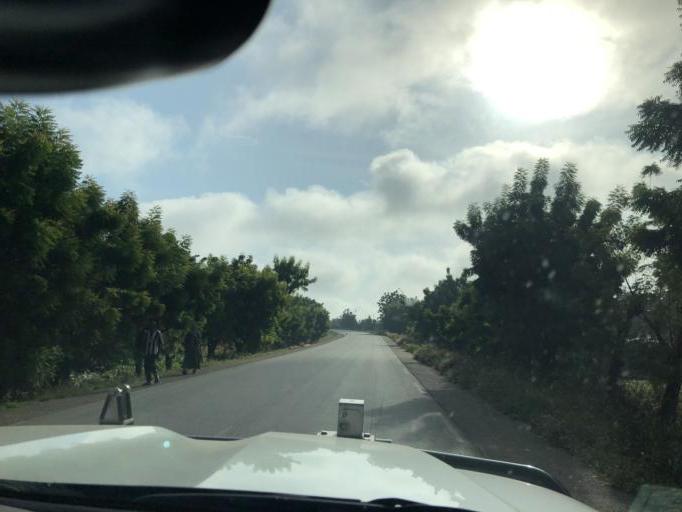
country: CM
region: North Province
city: Pitoa
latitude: 9.4938
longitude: 13.6855
